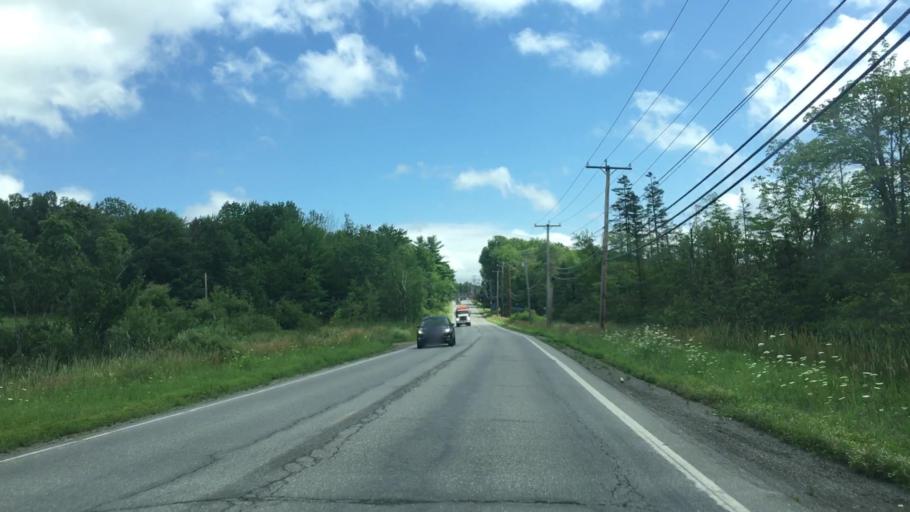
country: US
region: Maine
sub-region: Penobscot County
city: Hermon
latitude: 44.8090
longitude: -68.9196
